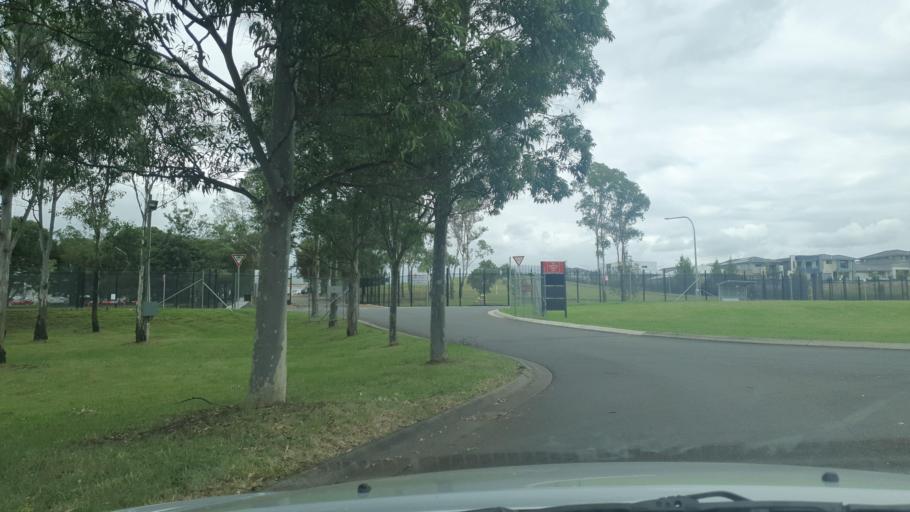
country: AU
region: New South Wales
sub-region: Penrith Municipality
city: Werrington County
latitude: -33.7711
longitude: 150.7421
